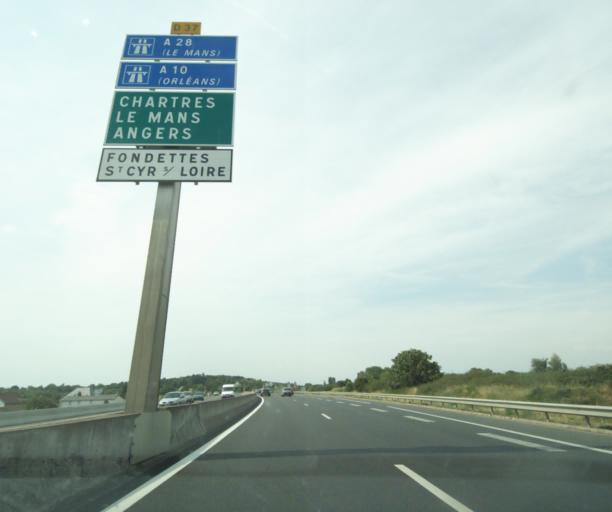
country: FR
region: Centre
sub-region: Departement d'Indre-et-Loire
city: La Riche
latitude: 47.3850
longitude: 0.6508
